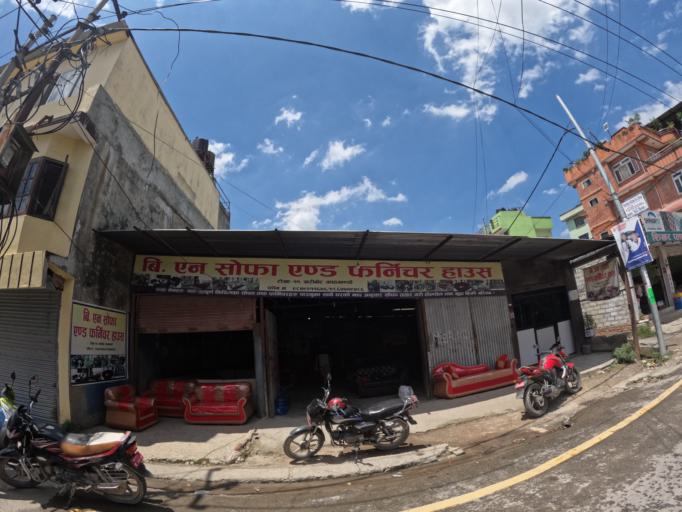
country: NP
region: Central Region
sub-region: Bagmati Zone
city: Kathmandu
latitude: 27.7427
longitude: 85.3223
